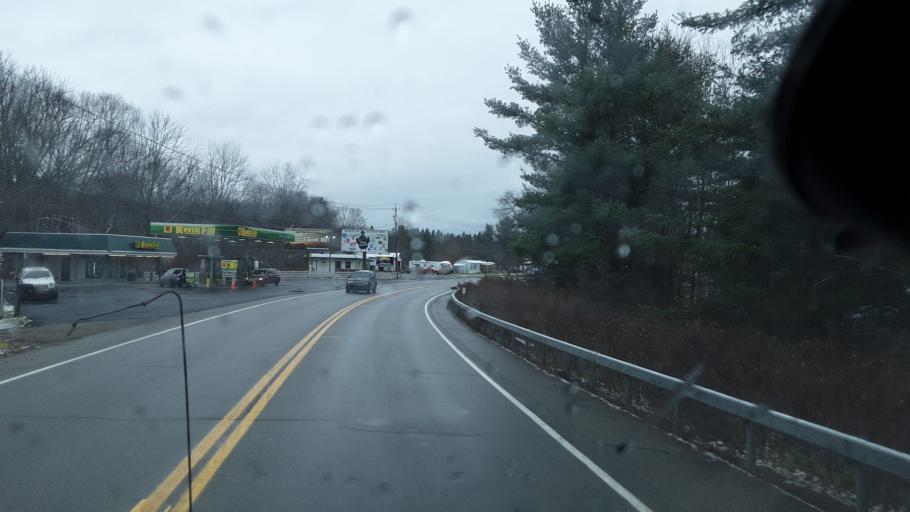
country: US
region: New York
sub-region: Cattaraugus County
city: Westons Mills
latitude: 42.0565
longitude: -78.3697
